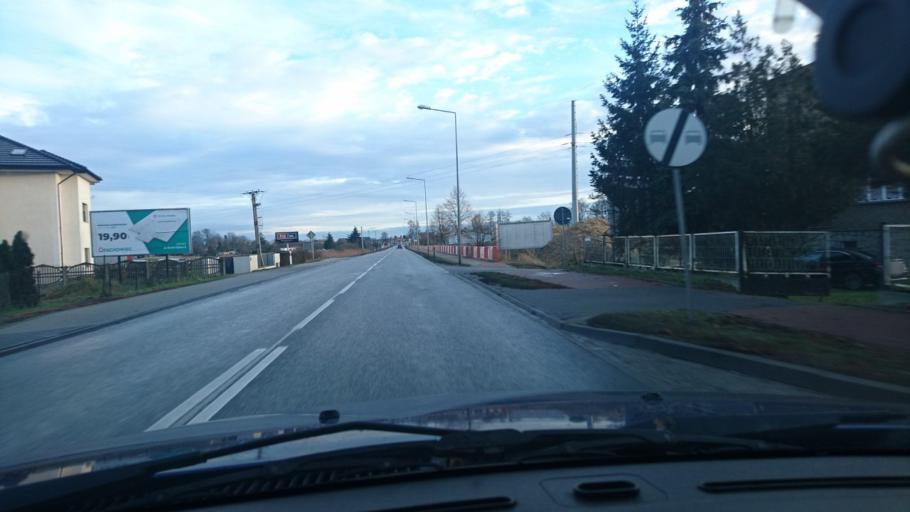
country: PL
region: Greater Poland Voivodeship
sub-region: Powiat kepinski
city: Kepno
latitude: 51.2715
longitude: 17.9933
